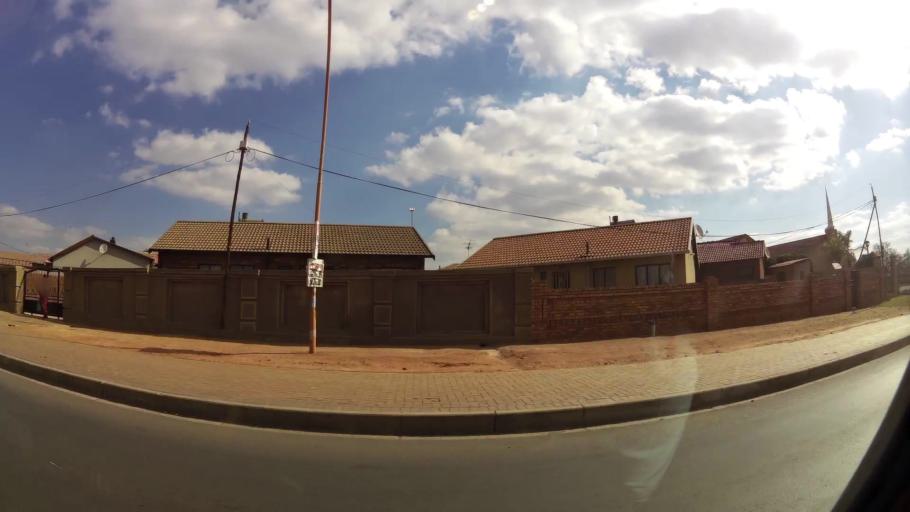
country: ZA
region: Gauteng
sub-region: Ekurhuleni Metropolitan Municipality
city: Tembisa
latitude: -25.9922
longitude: 28.2449
